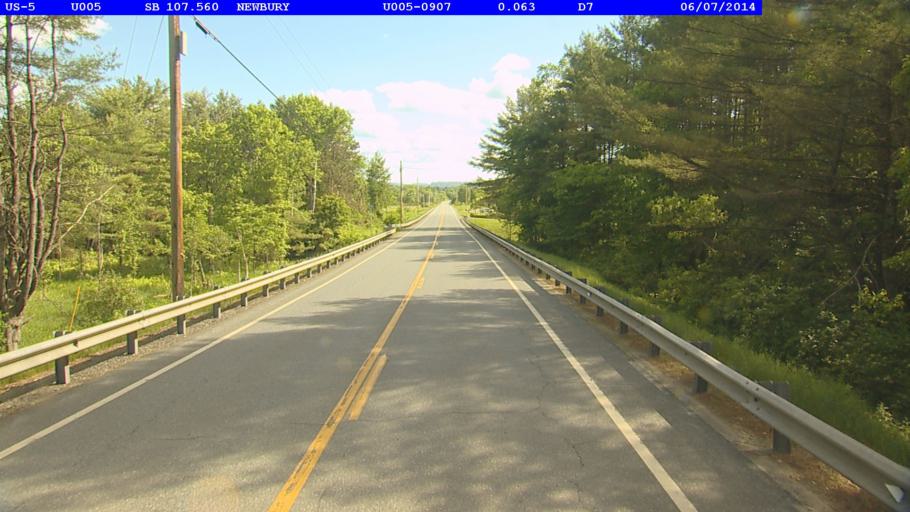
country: US
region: New Hampshire
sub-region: Grafton County
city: Haverhill
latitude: 44.0338
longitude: -72.0899
